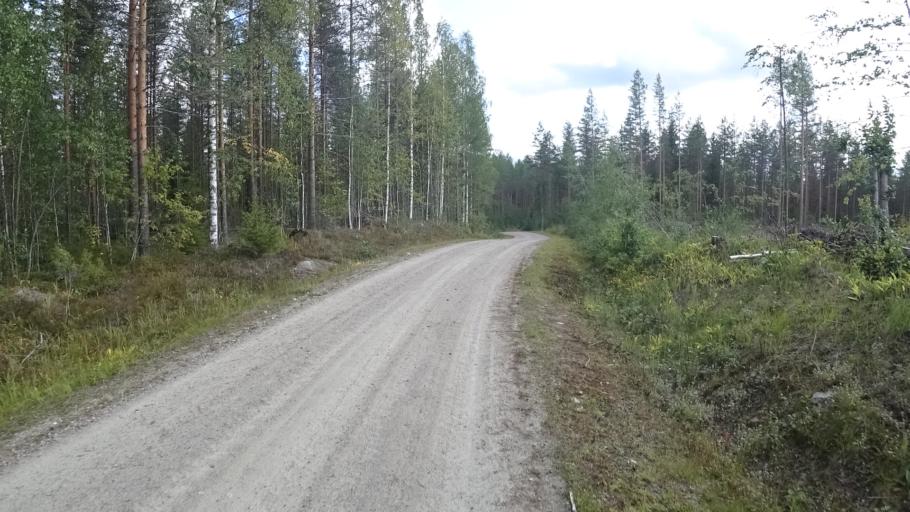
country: FI
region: North Karelia
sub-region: Joensuu
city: Ilomantsi
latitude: 62.6190
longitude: 31.2299
